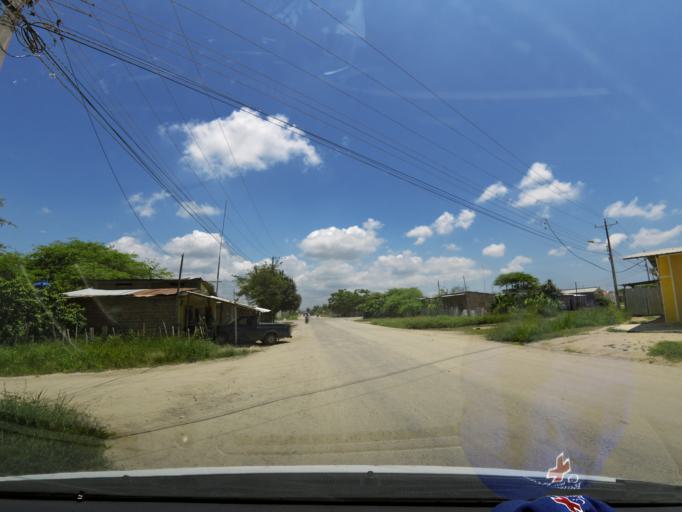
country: EC
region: El Oro
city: Huaquillas
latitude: -3.4786
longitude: -80.2097
